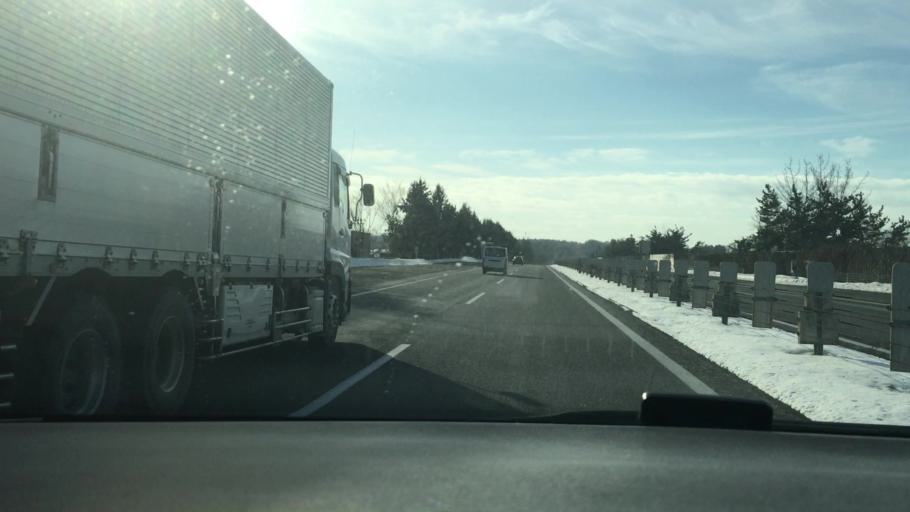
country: JP
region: Iwate
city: Hanamaki
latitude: 39.3814
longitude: 141.0922
